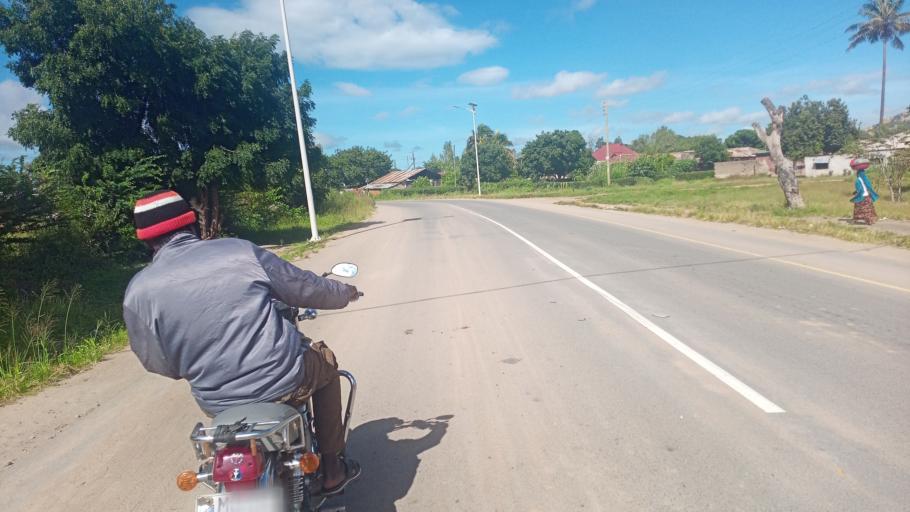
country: TZ
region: Dodoma
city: Dodoma
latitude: -6.1813
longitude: 35.7383
